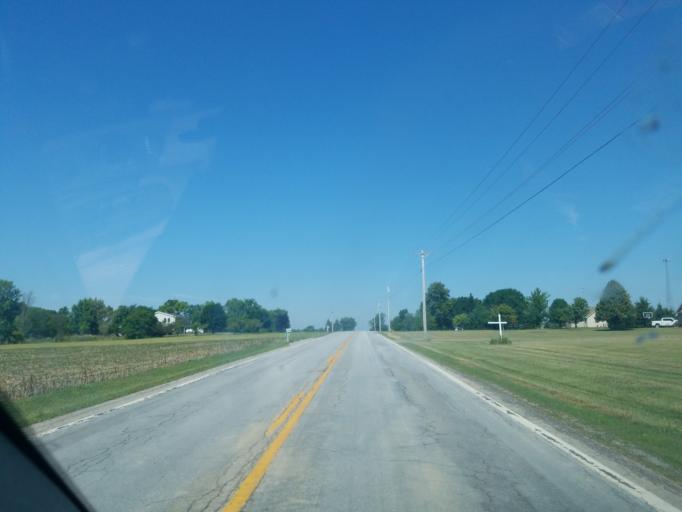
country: US
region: Ohio
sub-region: Logan County
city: Northwood
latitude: 40.4380
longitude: -83.7865
